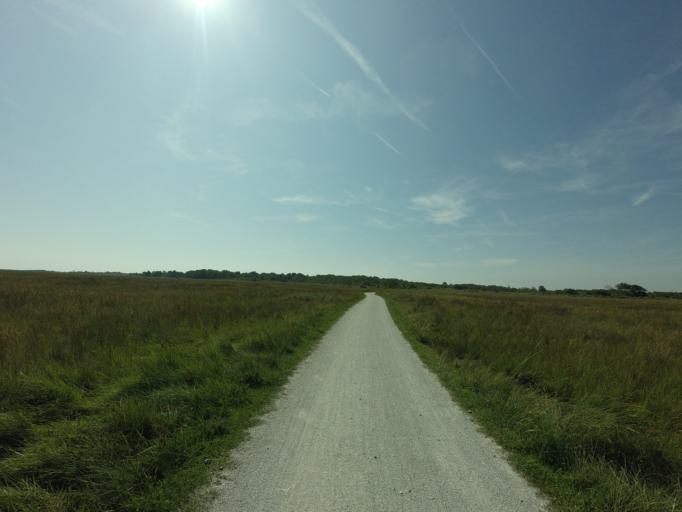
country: NL
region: Friesland
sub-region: Gemeente Schiermonnikoog
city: Schiermonnikoog
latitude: 53.4861
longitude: 6.2058
